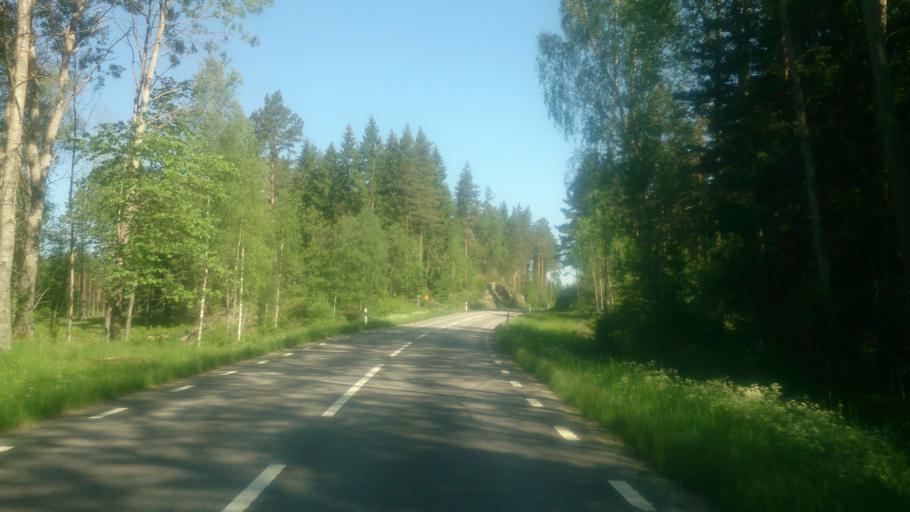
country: SE
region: OEstergoetland
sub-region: Atvidabergs Kommun
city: Atvidaberg
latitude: 58.1215
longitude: 16.0946
